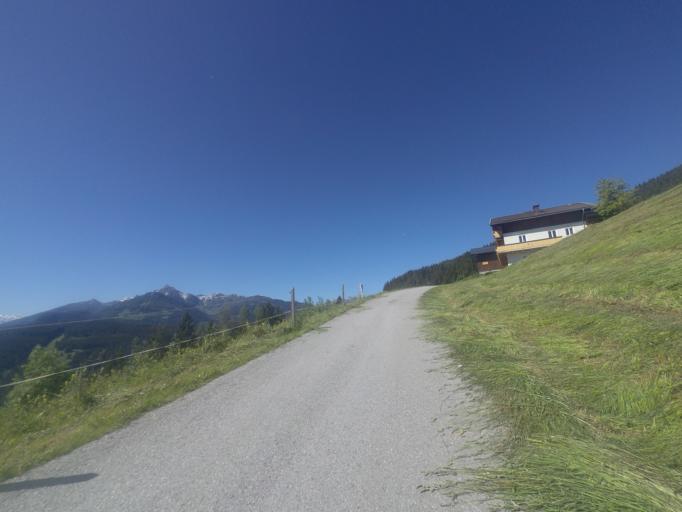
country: AT
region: Salzburg
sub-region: Politischer Bezirk Zell am See
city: Lend
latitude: 47.3275
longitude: 13.0585
